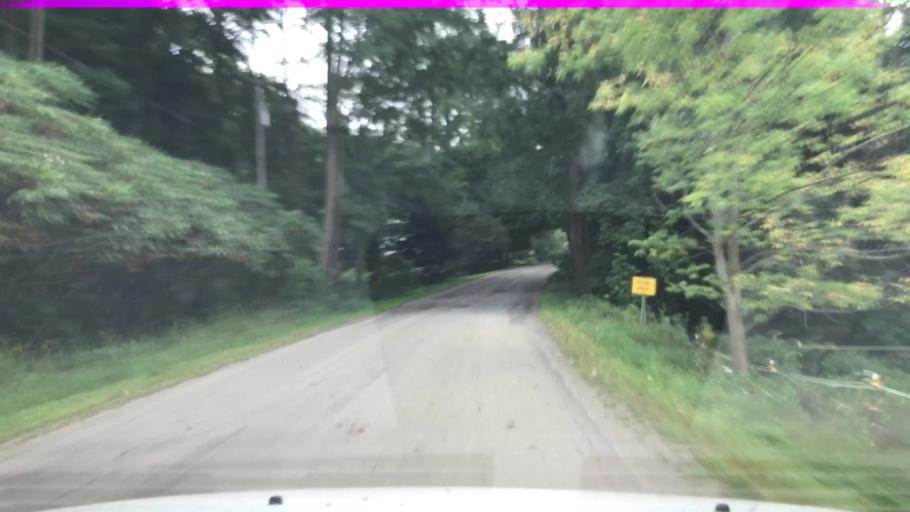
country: US
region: New York
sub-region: Cattaraugus County
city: Little Valley
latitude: 42.3123
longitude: -78.7194
